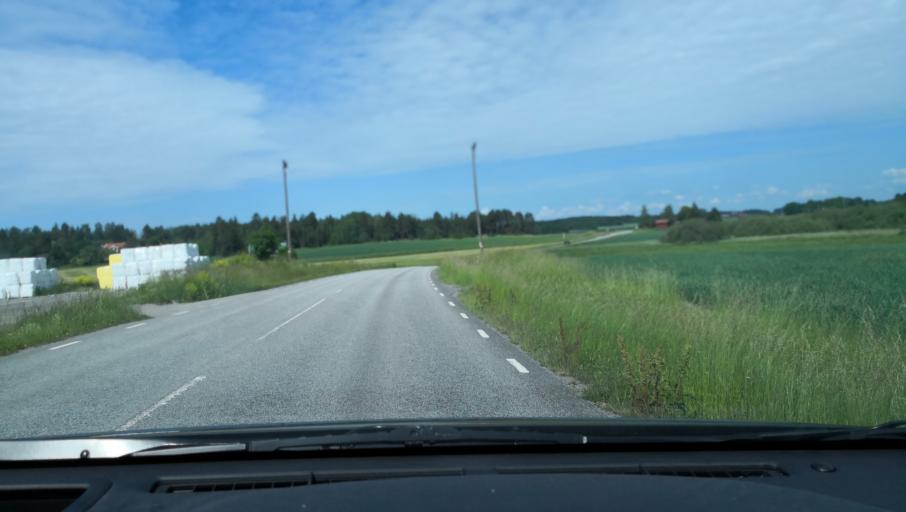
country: SE
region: Stockholm
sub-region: Sigtuna Kommun
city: Sigtuna
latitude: 59.6605
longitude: 17.6898
